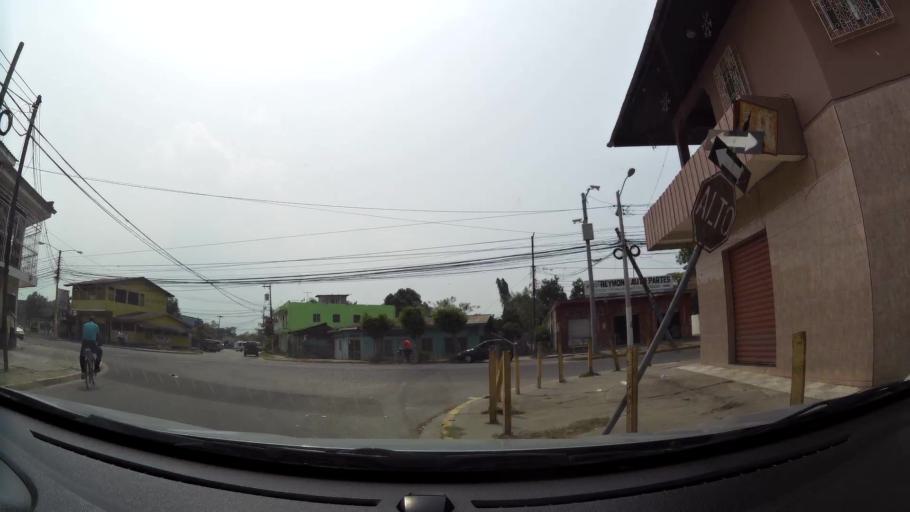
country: HN
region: Cortes
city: La Lima
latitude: 15.4378
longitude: -87.9315
